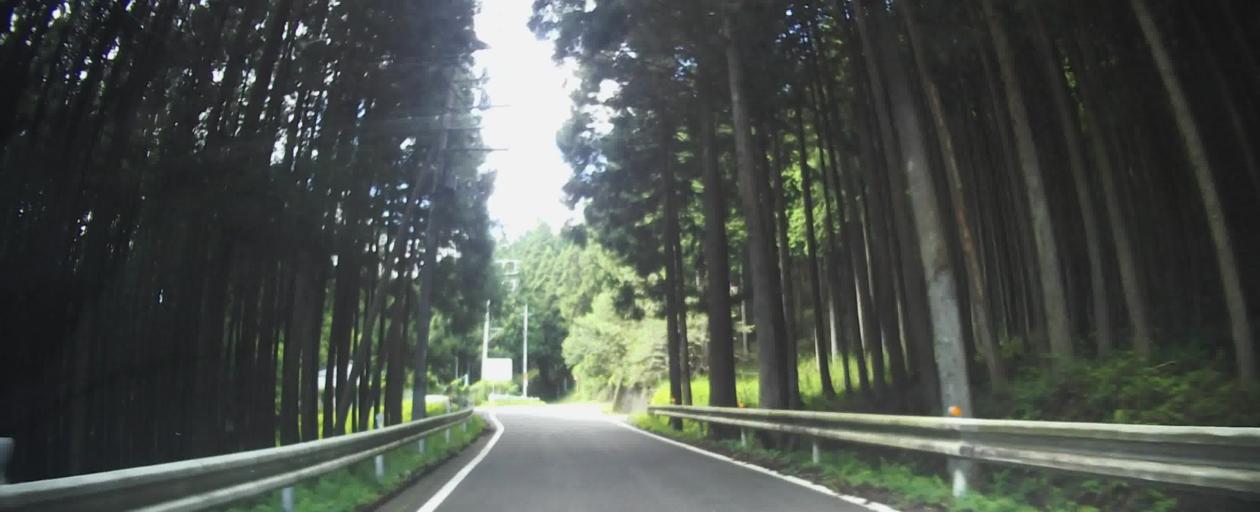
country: JP
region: Gunma
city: Kanekomachi
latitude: 36.4507
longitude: 138.9029
